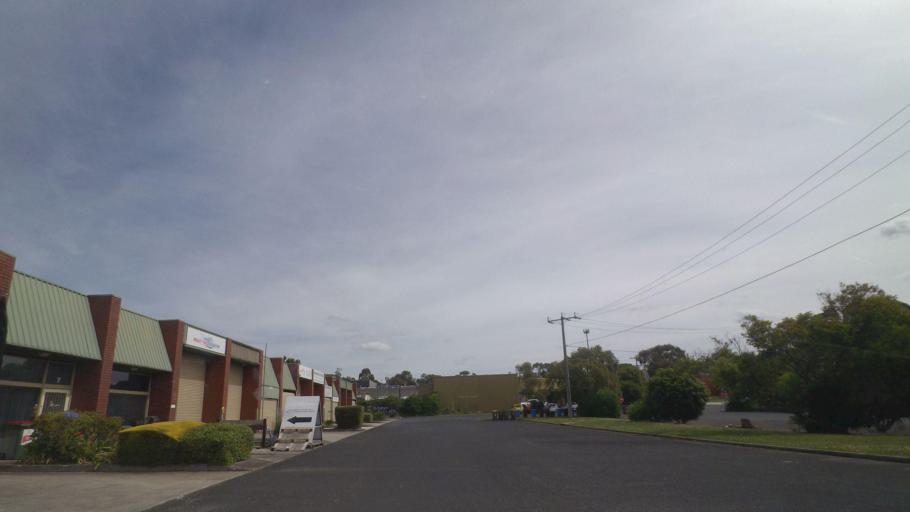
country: AU
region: Victoria
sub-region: Maroondah
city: Bayswater North
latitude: -37.8352
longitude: 145.2904
